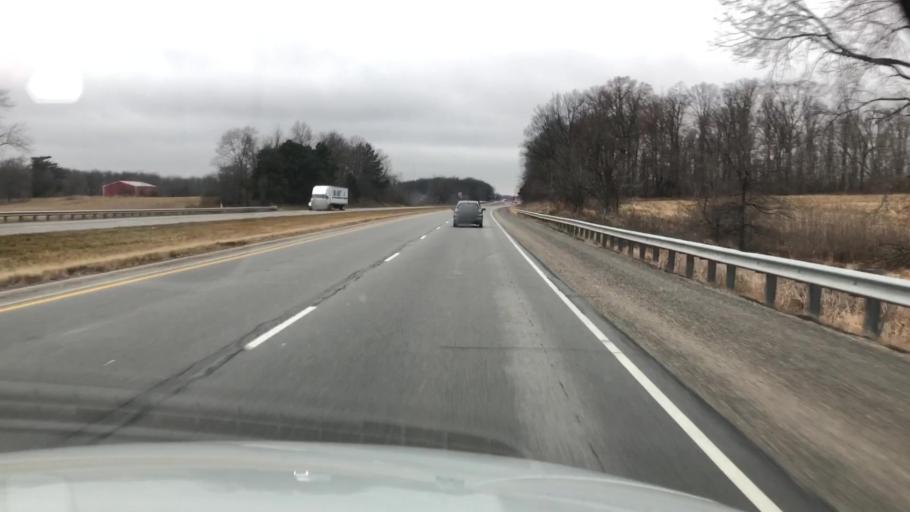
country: US
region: Indiana
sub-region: Whitley County
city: Churubusco
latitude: 41.1259
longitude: -85.3263
